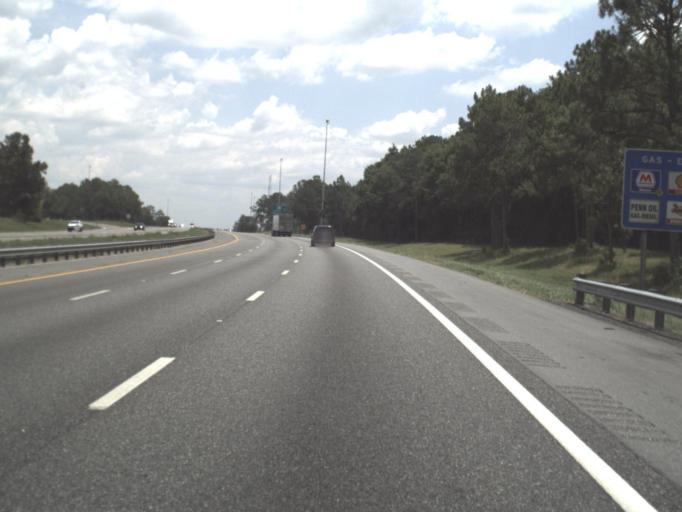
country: US
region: Florida
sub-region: Hamilton County
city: Jasper
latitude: 30.5217
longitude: -83.0640
